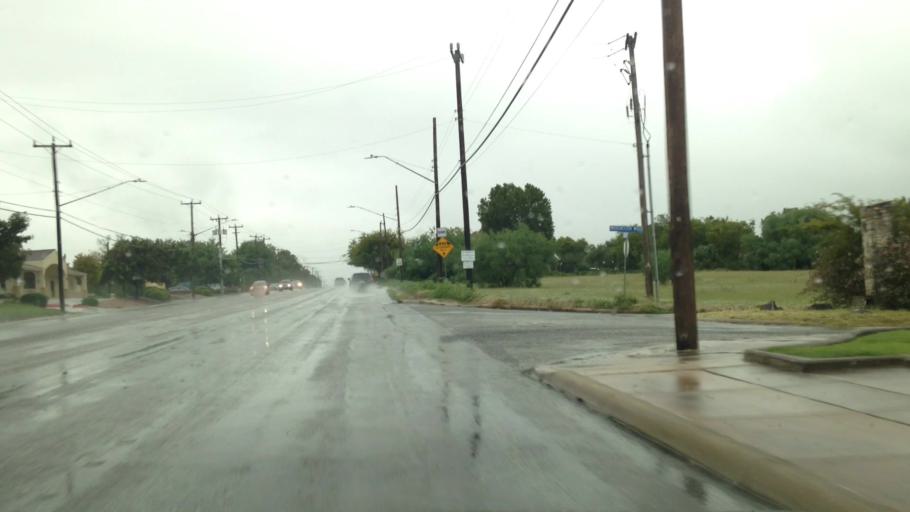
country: US
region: Texas
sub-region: Bexar County
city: Live Oak
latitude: 29.5710
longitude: -98.3677
